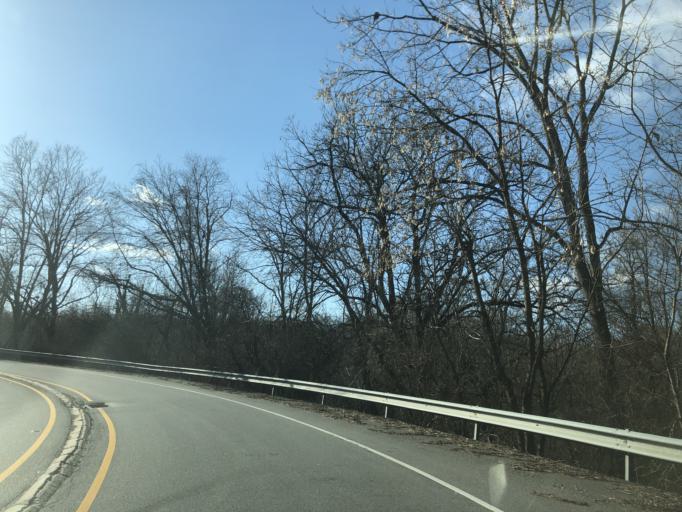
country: US
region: Pennsylvania
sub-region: Chester County
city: Coatesville
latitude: 40.0023
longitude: -75.8223
